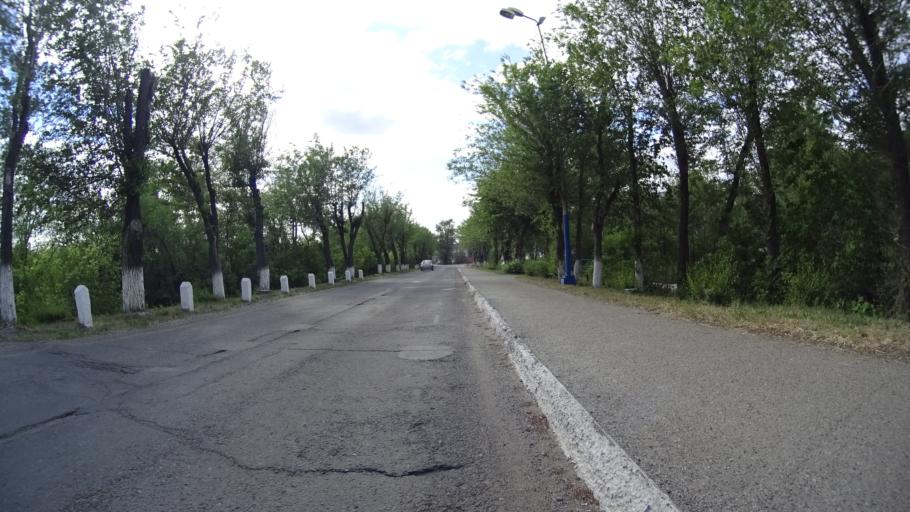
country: RU
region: Chelyabinsk
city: Troitsk
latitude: 54.0406
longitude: 61.6390
